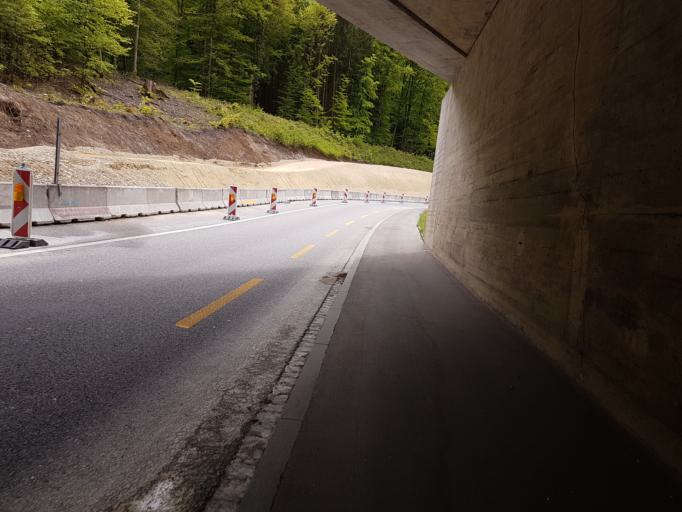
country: CH
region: Aargau
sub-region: Bezirk Brugg
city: Hausen
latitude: 47.4686
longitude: 8.1885
